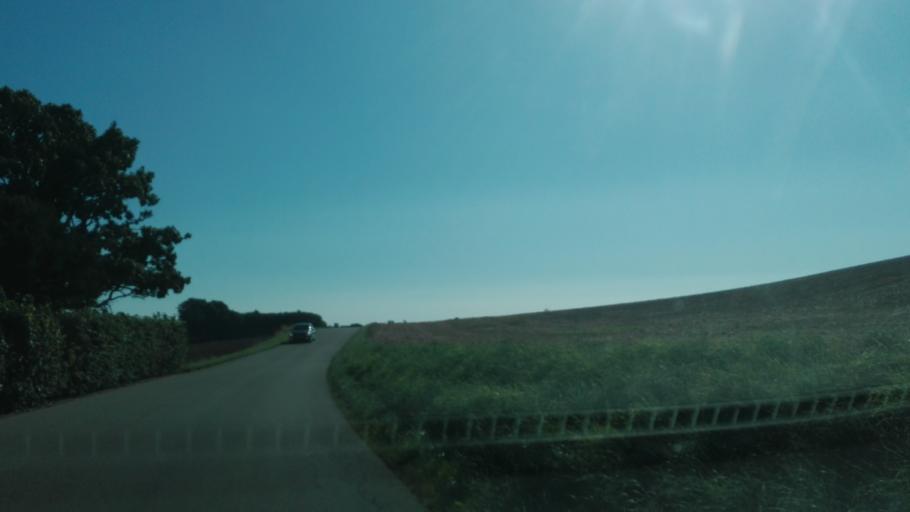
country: DK
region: Central Jutland
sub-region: Syddjurs Kommune
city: Ebeltoft
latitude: 56.2218
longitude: 10.7202
